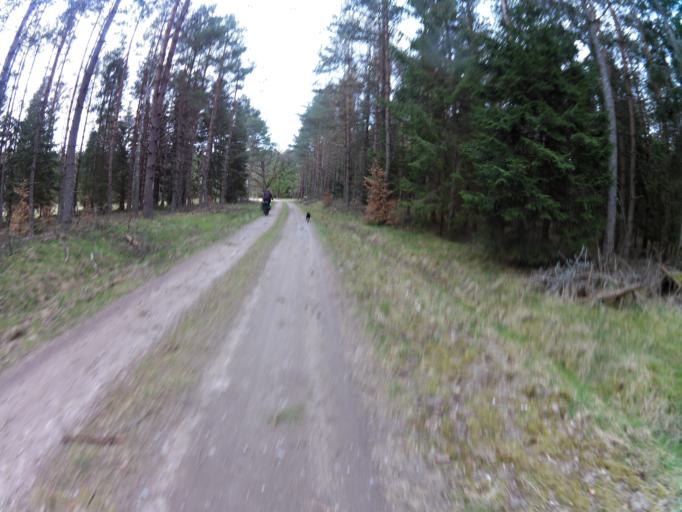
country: PL
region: West Pomeranian Voivodeship
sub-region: Powiat szczecinecki
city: Bialy Bor
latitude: 53.8836
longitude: 16.7200
